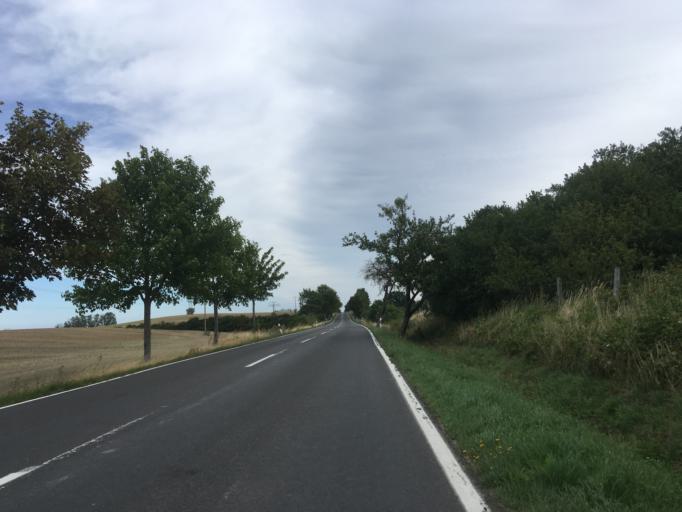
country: DE
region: Brandenburg
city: Mittenwalde
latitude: 53.2162
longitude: 13.5710
